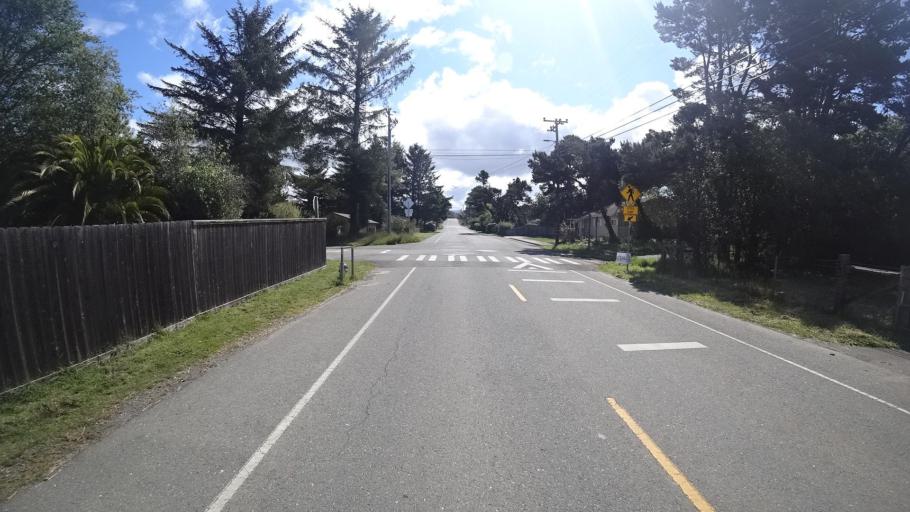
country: US
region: California
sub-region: Humboldt County
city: McKinleyville
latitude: 40.9417
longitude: -124.1207
